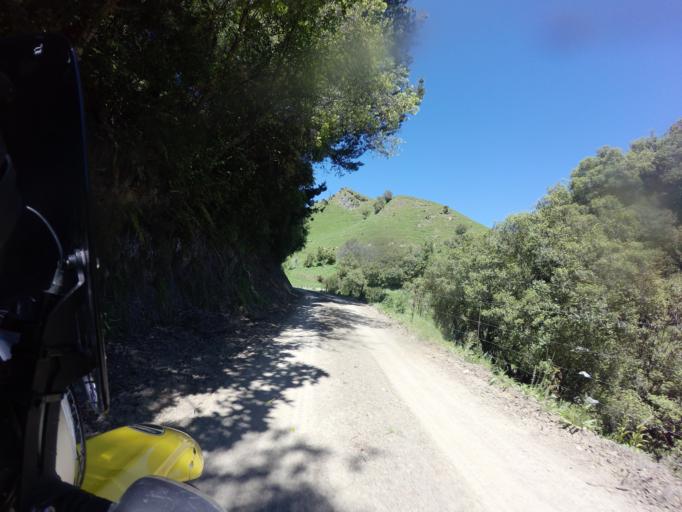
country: NZ
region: Bay of Plenty
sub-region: Opotiki District
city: Opotiki
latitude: -38.4043
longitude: 177.4528
